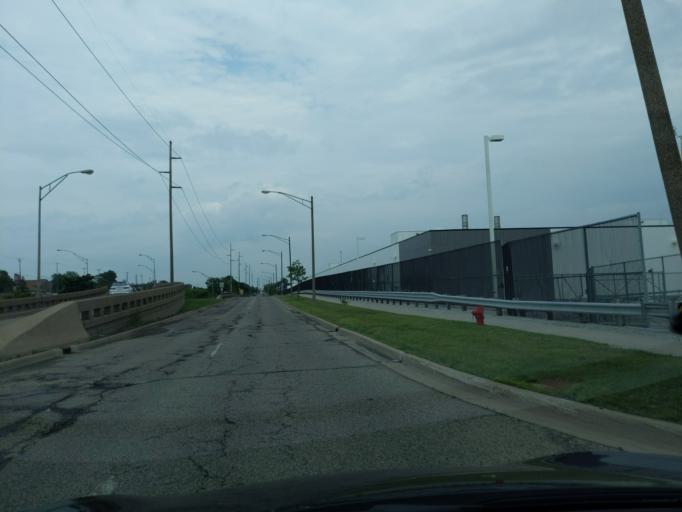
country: US
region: Michigan
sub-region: Ingham County
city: Lansing
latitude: 42.7255
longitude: -84.5651
